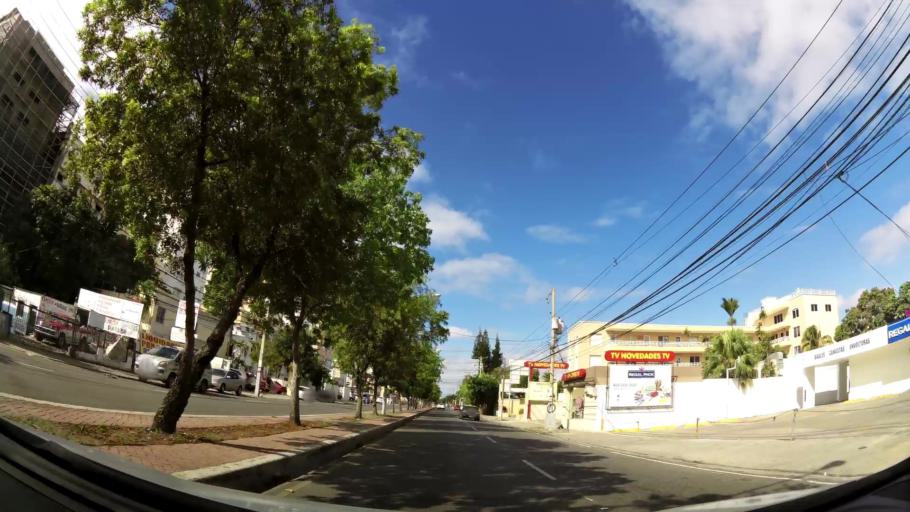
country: DO
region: Nacional
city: Bella Vista
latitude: 18.4566
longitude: -69.9413
